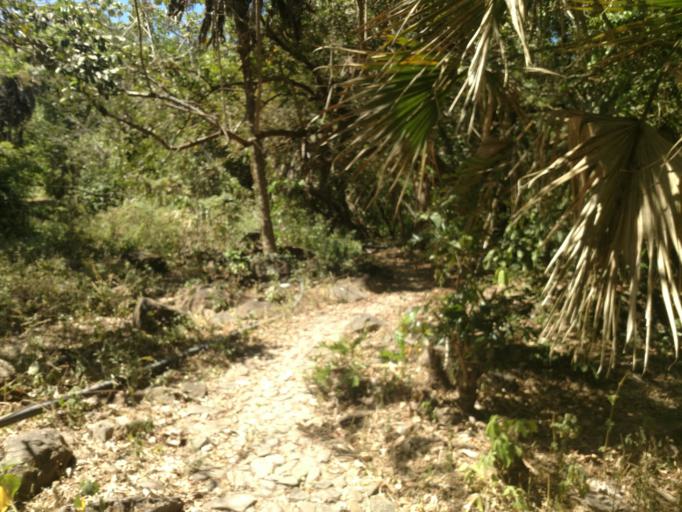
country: MX
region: Nayarit
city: Tepic
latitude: 21.5668
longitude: -104.9993
